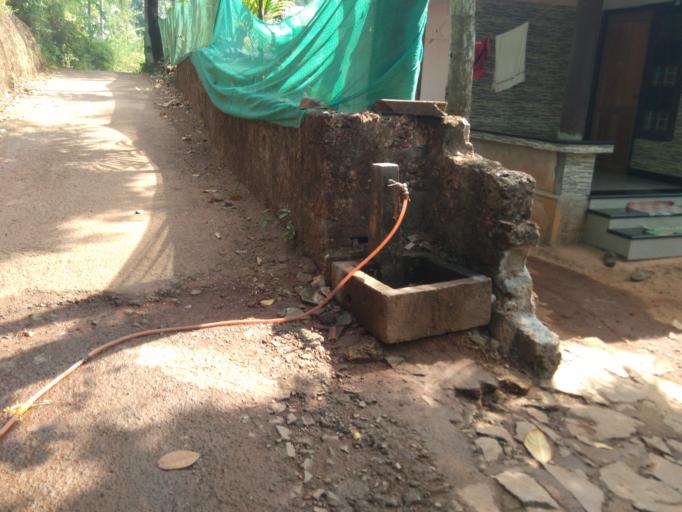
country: IN
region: Kerala
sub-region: Kozhikode
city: Kunnamangalam
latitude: 11.2879
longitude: 75.8331
